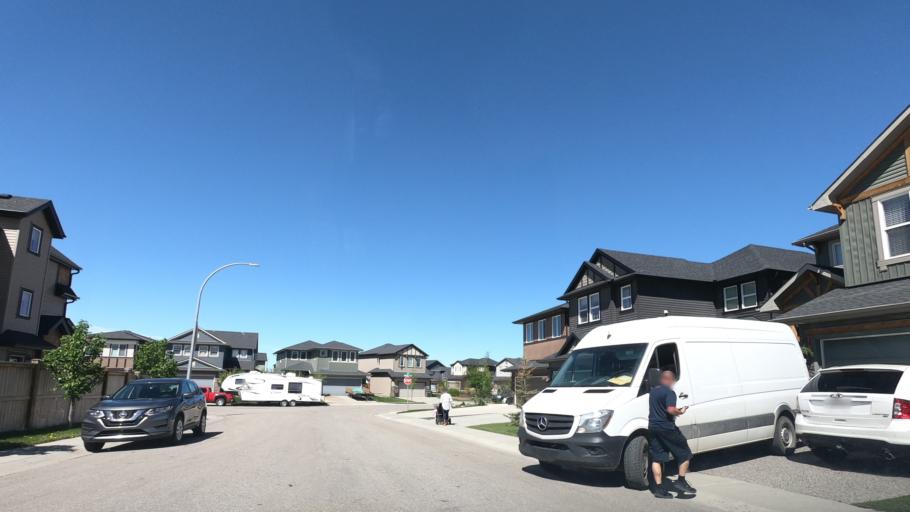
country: CA
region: Alberta
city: Airdrie
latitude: 51.2655
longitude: -113.9742
